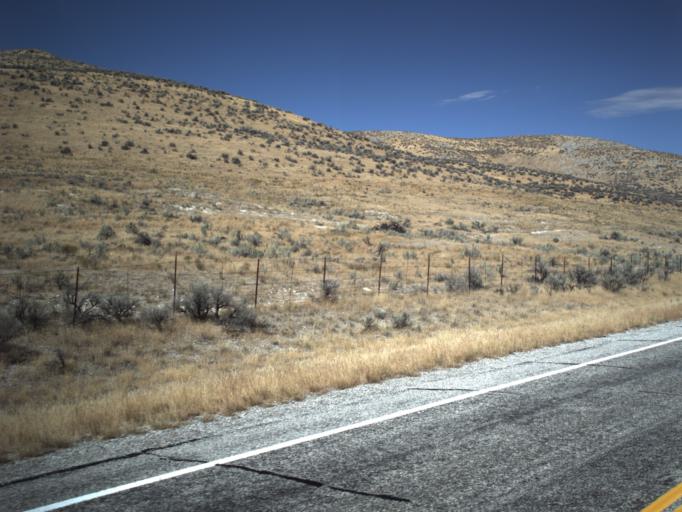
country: US
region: Utah
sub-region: Box Elder County
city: Tremonton
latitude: 41.6955
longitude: -112.4449
